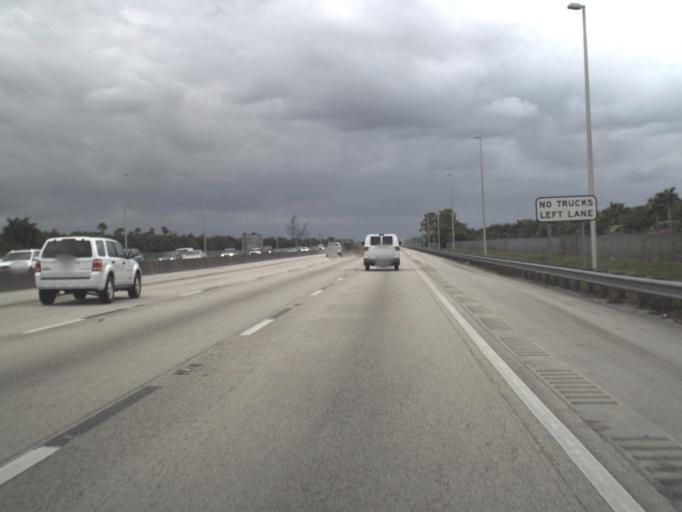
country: US
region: Florida
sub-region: Palm Beach County
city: Villages of Oriole
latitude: 26.5185
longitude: -80.1727
